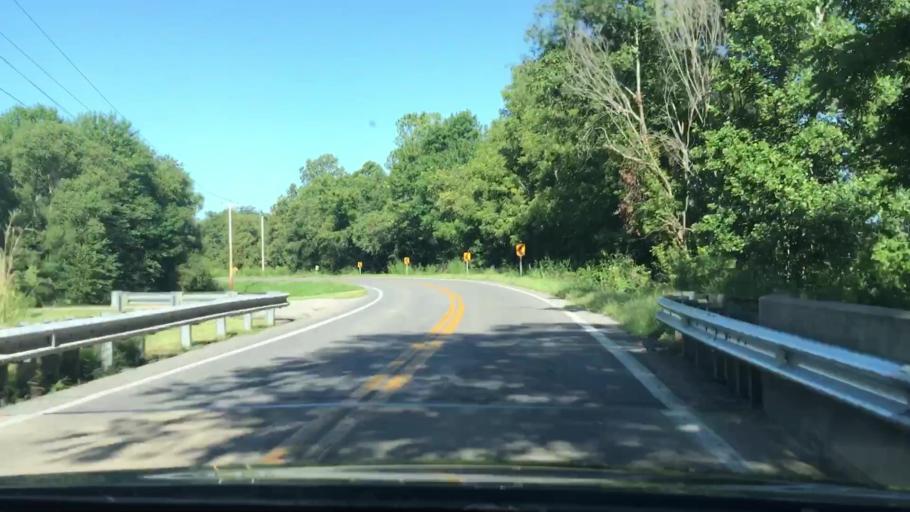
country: US
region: Kentucky
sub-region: Graves County
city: Mayfield
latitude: 36.7819
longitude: -88.5260
